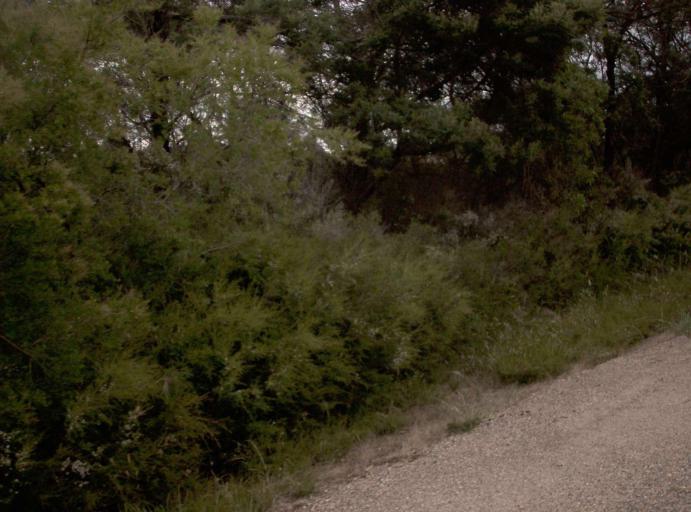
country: AU
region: Victoria
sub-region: East Gippsland
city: Bairnsdale
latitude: -37.9914
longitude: 147.3957
